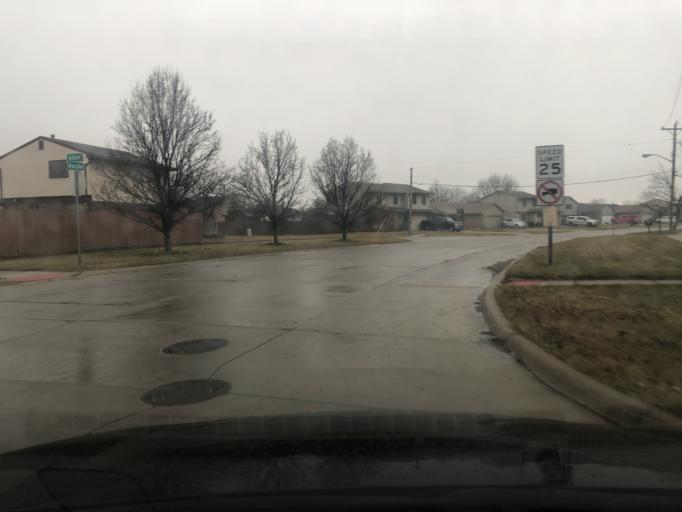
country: US
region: Michigan
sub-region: Wayne County
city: Gibraltar
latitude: 42.1036
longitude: -83.2248
